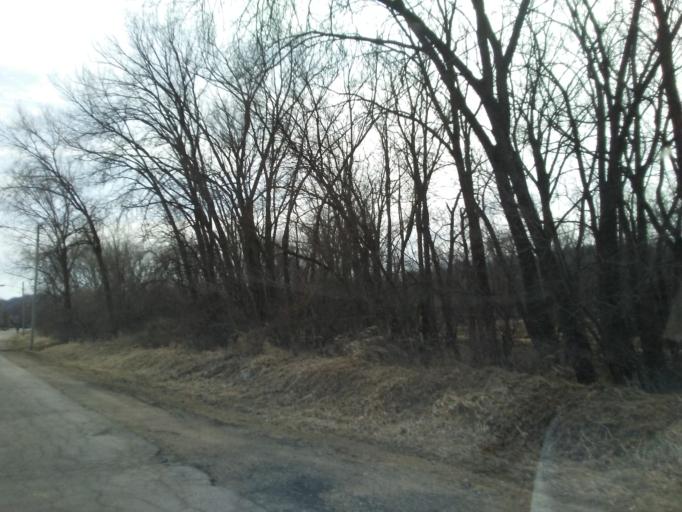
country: US
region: Iowa
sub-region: Winneshiek County
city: Decorah
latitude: 43.3125
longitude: -91.8096
